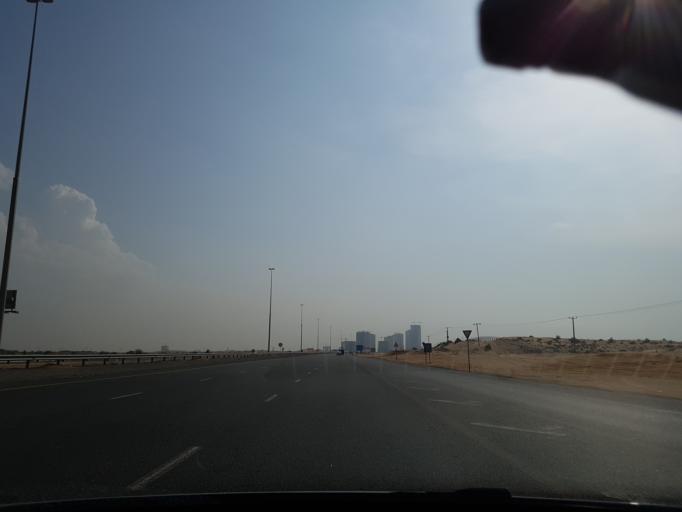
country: AE
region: Umm al Qaywayn
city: Umm al Qaywayn
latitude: 25.4170
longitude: 55.5885
